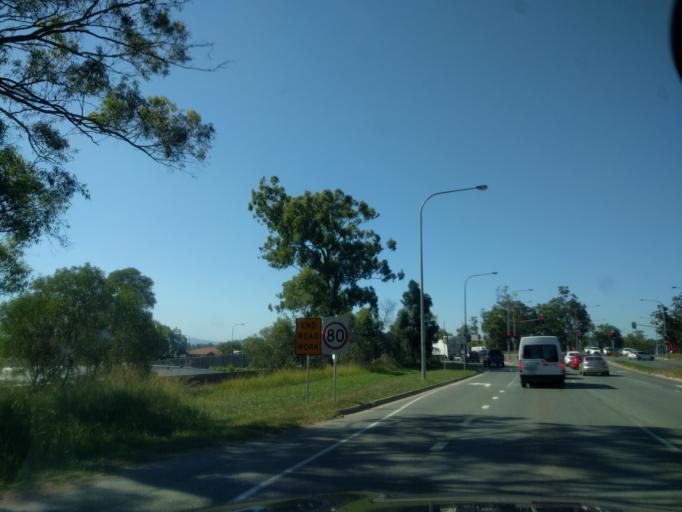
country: AU
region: Queensland
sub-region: Brisbane
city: Sunnybank Hills
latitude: -27.6393
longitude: 153.0447
